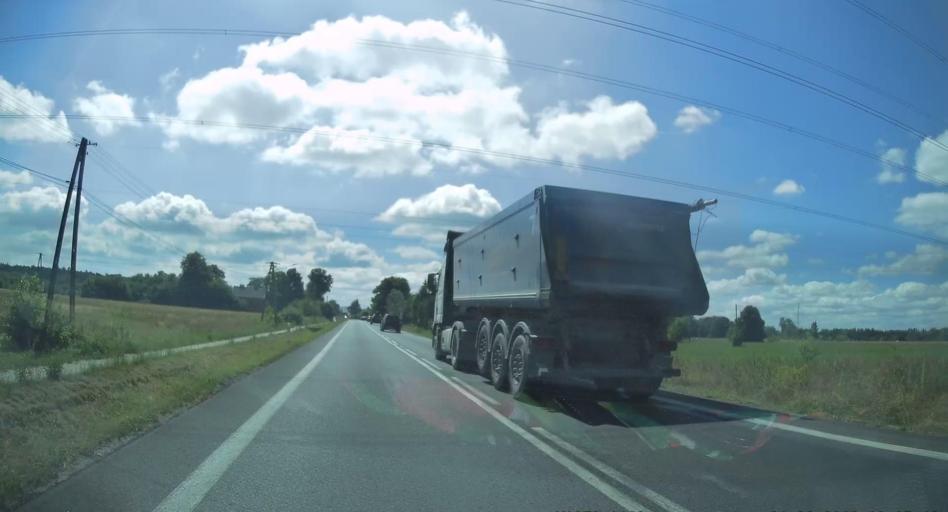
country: PL
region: Subcarpathian Voivodeship
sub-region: Powiat debicki
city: Brzeznica
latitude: 50.1272
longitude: 21.4854
